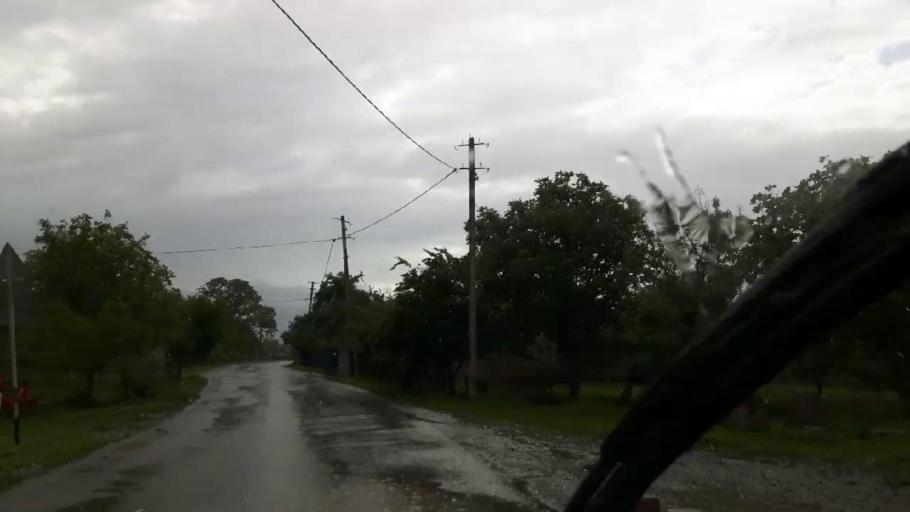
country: GE
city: Agara
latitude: 42.0103
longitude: 43.7652
